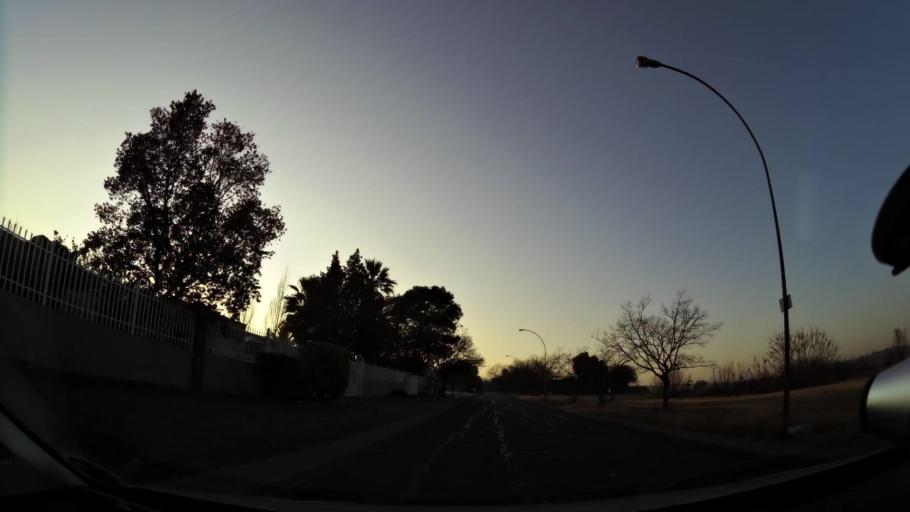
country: ZA
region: Orange Free State
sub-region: Mangaung Metropolitan Municipality
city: Bloemfontein
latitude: -29.1070
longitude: 26.1508
